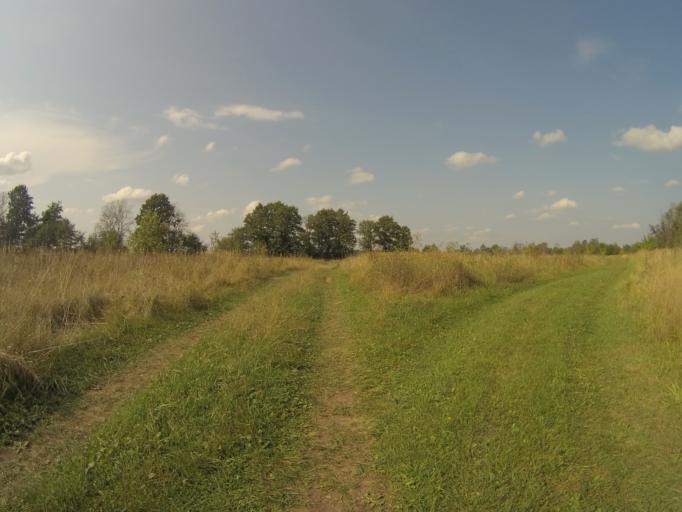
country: RU
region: Vladimir
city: Raduzhnyy
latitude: 56.0345
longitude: 40.2905
